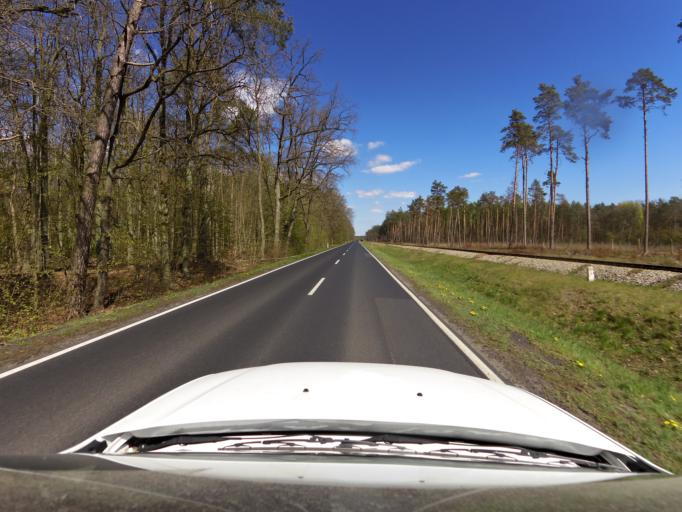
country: PL
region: West Pomeranian Voivodeship
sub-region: Powiat mysliborski
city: Debno
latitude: 52.7499
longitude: 14.7240
